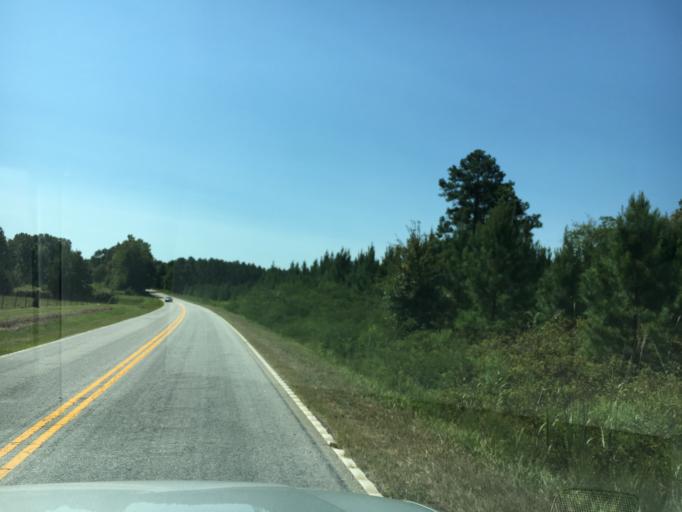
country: US
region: South Carolina
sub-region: Laurens County
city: Joanna
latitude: 34.3623
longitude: -81.8611
